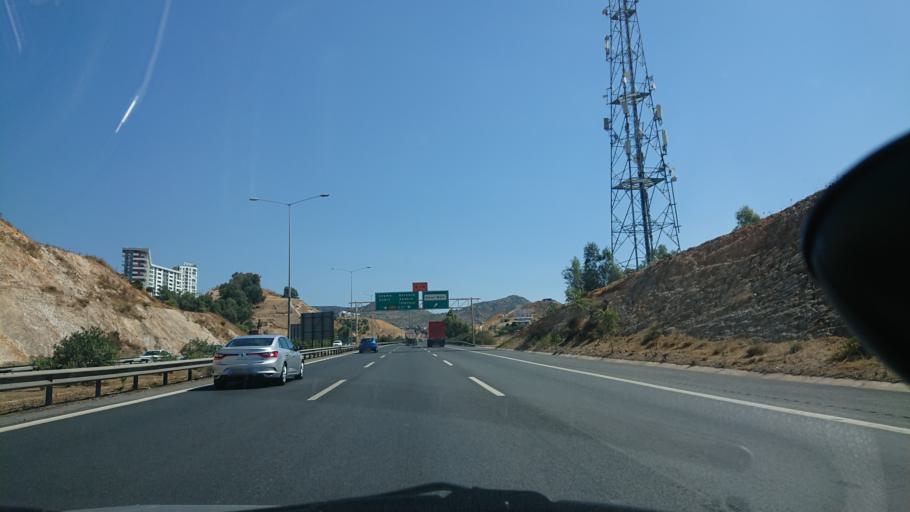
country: TR
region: Izmir
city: Karsiyaka
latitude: 38.4861
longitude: 27.1249
